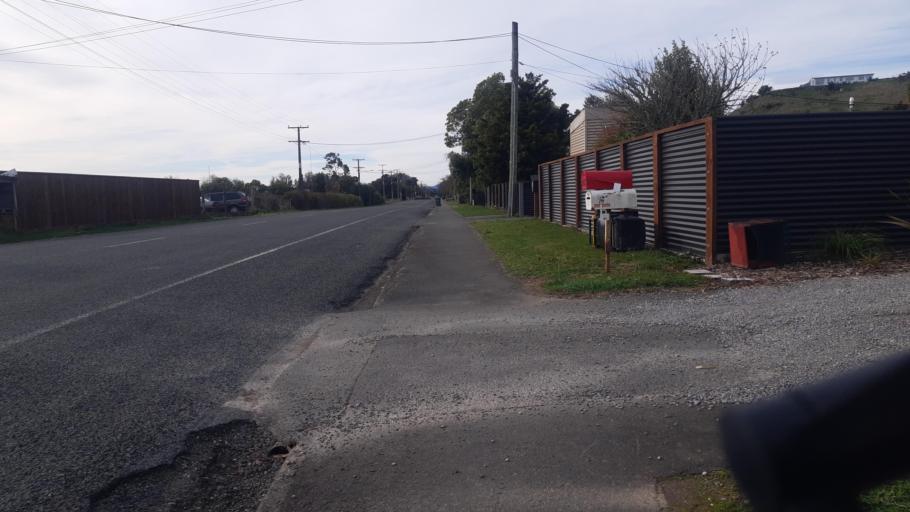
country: NZ
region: Tasman
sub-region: Tasman District
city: Brightwater
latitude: -41.3808
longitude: 173.0970
